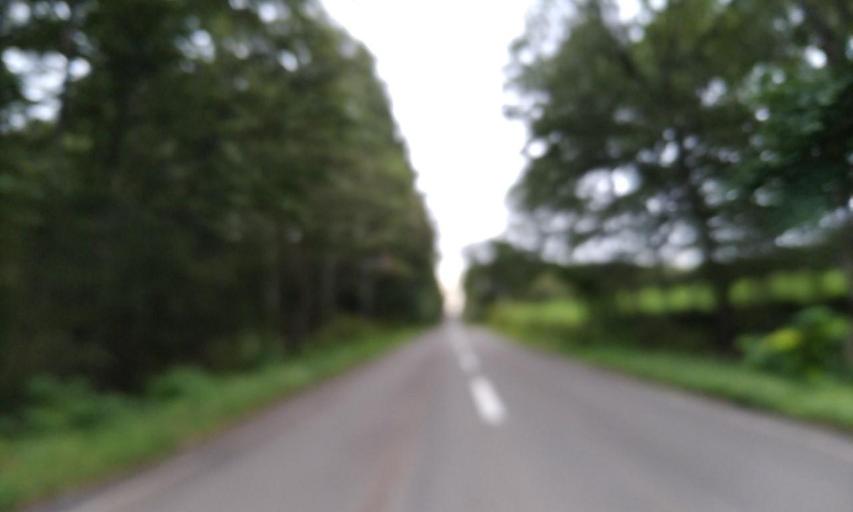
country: JP
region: Hokkaido
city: Obihiro
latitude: 42.6695
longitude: 143.0575
